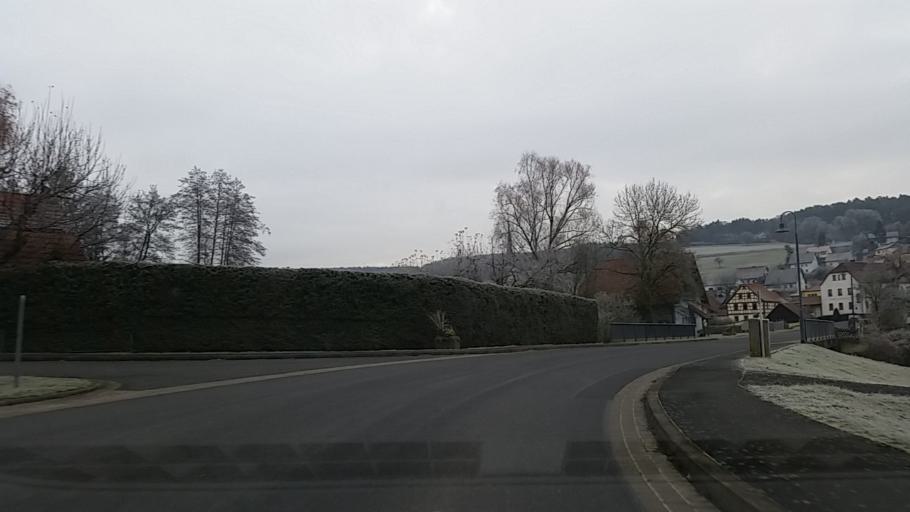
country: DE
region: Bavaria
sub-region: Regierungsbezirk Unterfranken
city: Eussenheim
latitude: 50.0143
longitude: 9.8630
